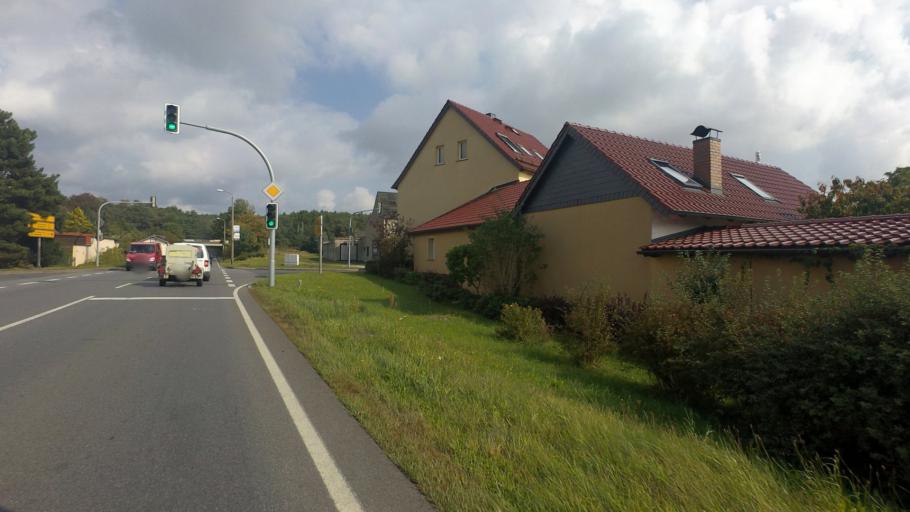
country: DE
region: Brandenburg
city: Elsterwerda
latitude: 51.4721
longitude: 13.4960
